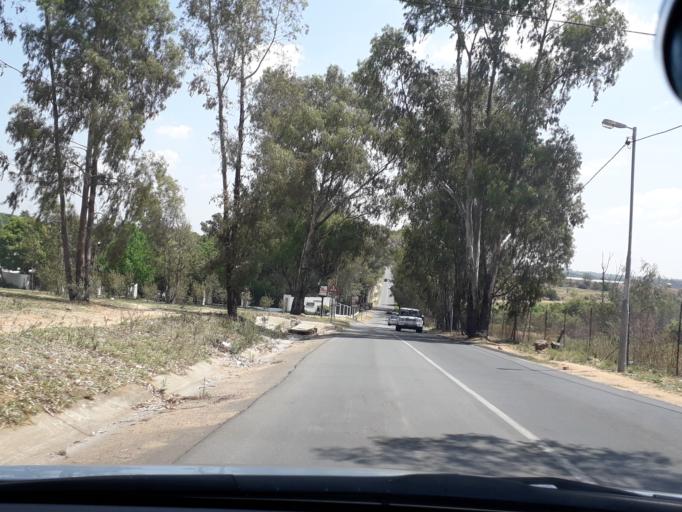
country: ZA
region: Gauteng
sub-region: City of Johannesburg Metropolitan Municipality
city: Midrand
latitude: -26.0173
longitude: 28.0715
